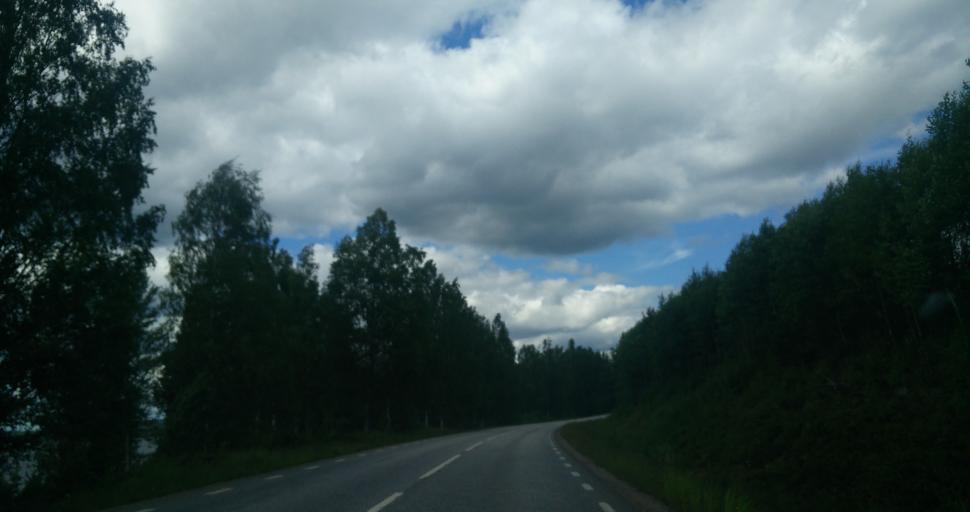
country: SE
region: Gaevleborg
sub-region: Nordanstigs Kommun
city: Bergsjoe
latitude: 62.0753
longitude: 16.8212
